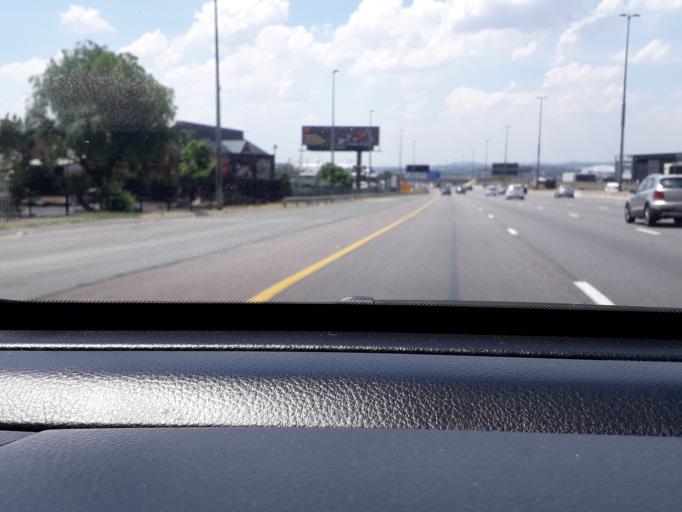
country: ZA
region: Gauteng
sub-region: City of Tshwane Metropolitan Municipality
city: Centurion
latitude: -25.8977
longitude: 28.1633
